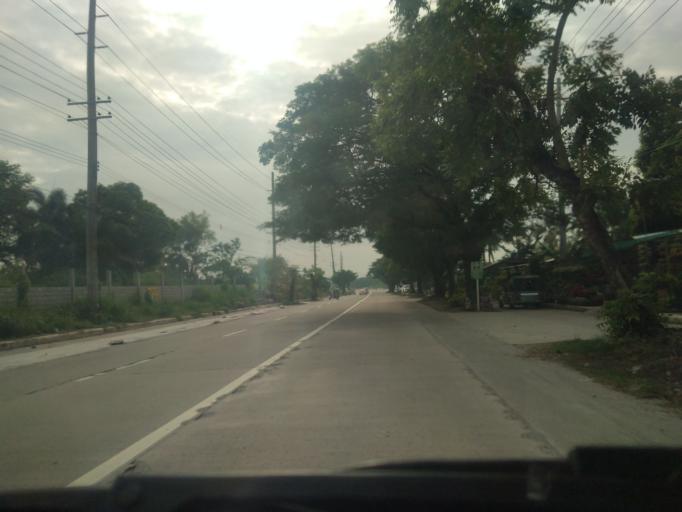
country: PH
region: Central Luzon
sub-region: Province of Pampanga
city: Calibutbut
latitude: 15.1204
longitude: 120.5886
